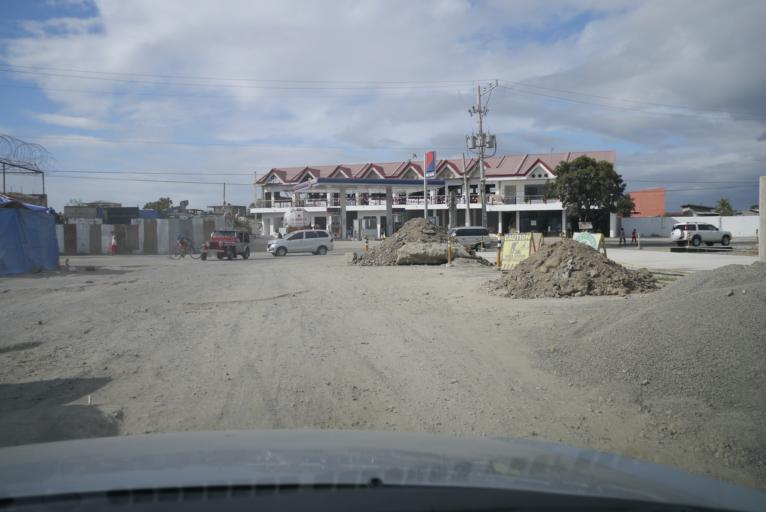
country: PH
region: Calabarzon
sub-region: Province of Rizal
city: Taytay
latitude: 14.5438
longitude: 121.1271
